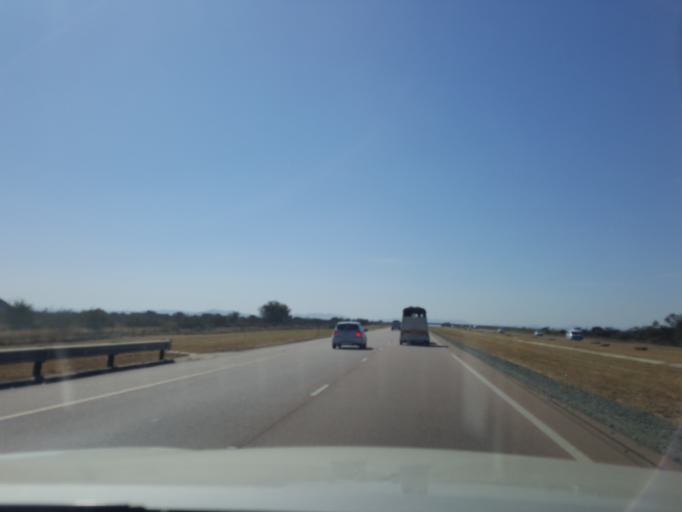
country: ZA
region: North-West
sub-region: Bojanala Platinum District Municipality
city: Brits
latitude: -25.7041
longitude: 27.7157
